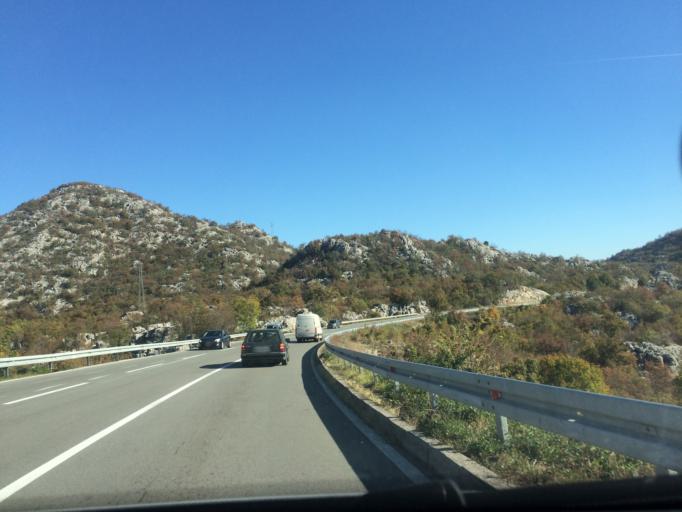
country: ME
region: Cetinje
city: Cetinje
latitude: 42.3774
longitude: 19.0383
